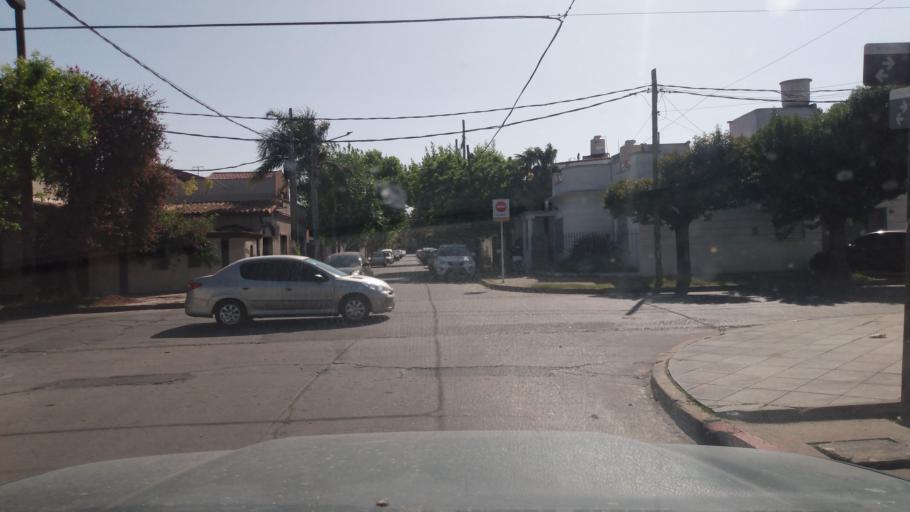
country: AR
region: Buenos Aires
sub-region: Partido de Moron
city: Moron
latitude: -34.6509
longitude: -58.5953
